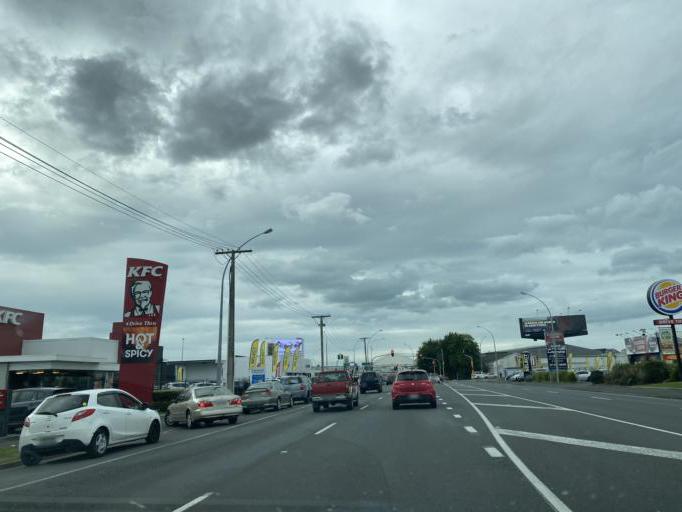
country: NZ
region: Waikato
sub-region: Hamilton City
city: Hamilton
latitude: -37.7903
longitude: 175.2599
